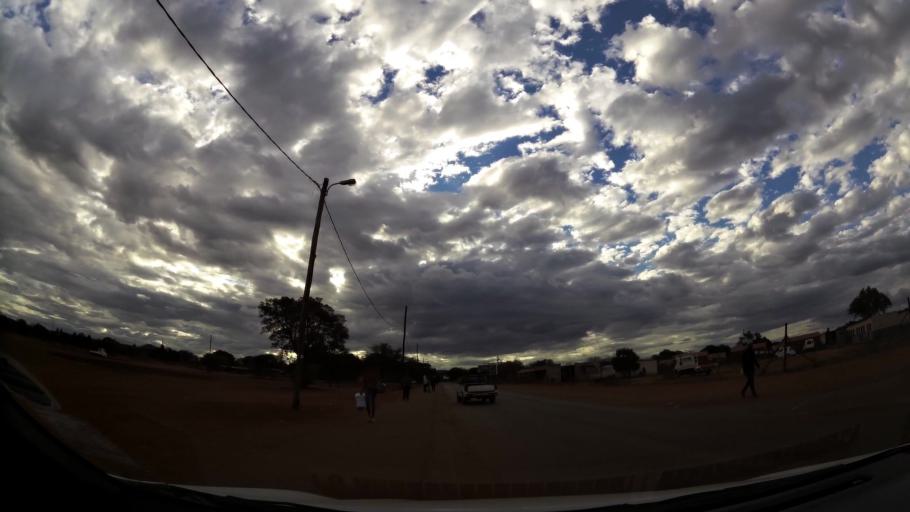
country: ZA
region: Limpopo
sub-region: Waterberg District Municipality
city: Modimolle
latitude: -24.5198
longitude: 28.7214
